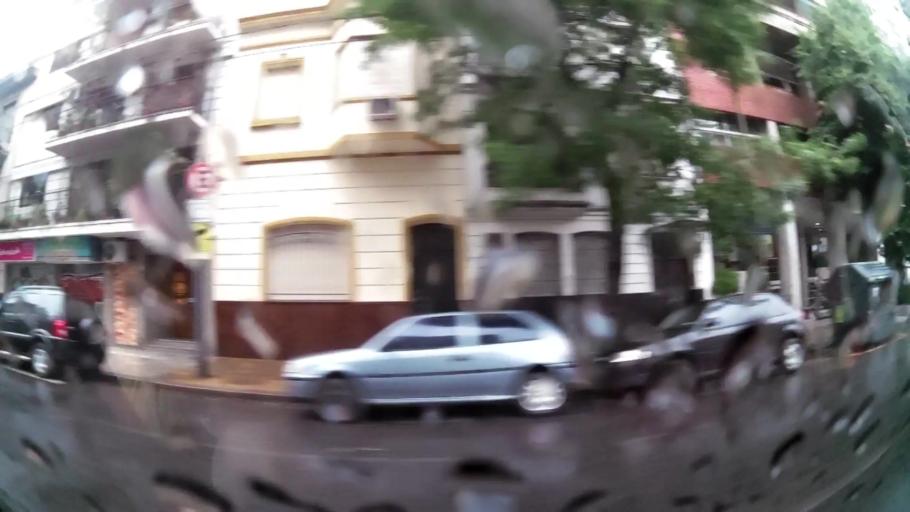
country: AR
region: Buenos Aires F.D.
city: Buenos Aires
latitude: -34.6312
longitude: -58.3724
